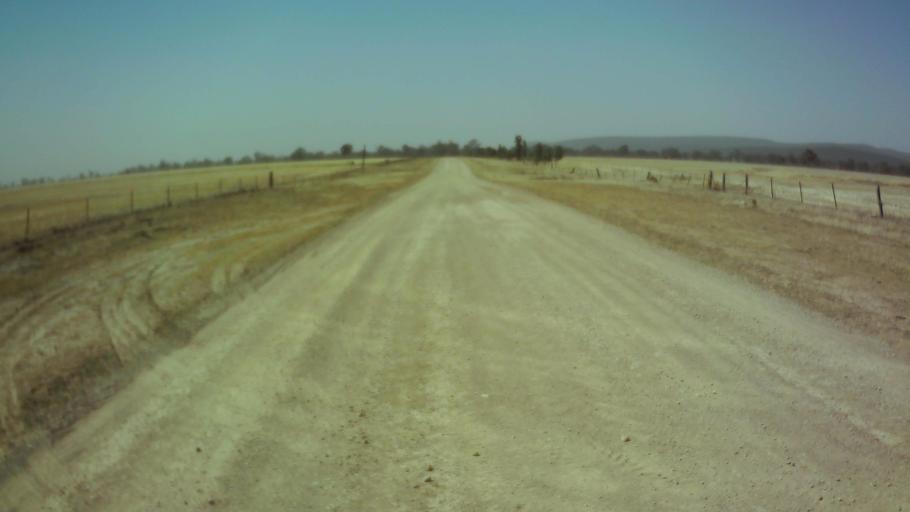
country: AU
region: New South Wales
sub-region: Weddin
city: Grenfell
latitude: -34.0141
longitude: 147.9157
